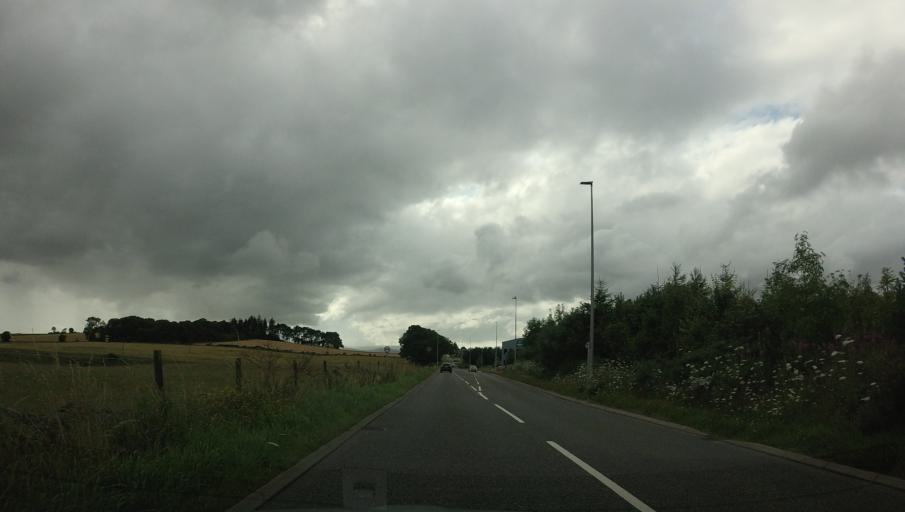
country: GB
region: Scotland
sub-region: Aberdeenshire
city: Westhill
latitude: 57.1443
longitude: -2.2850
